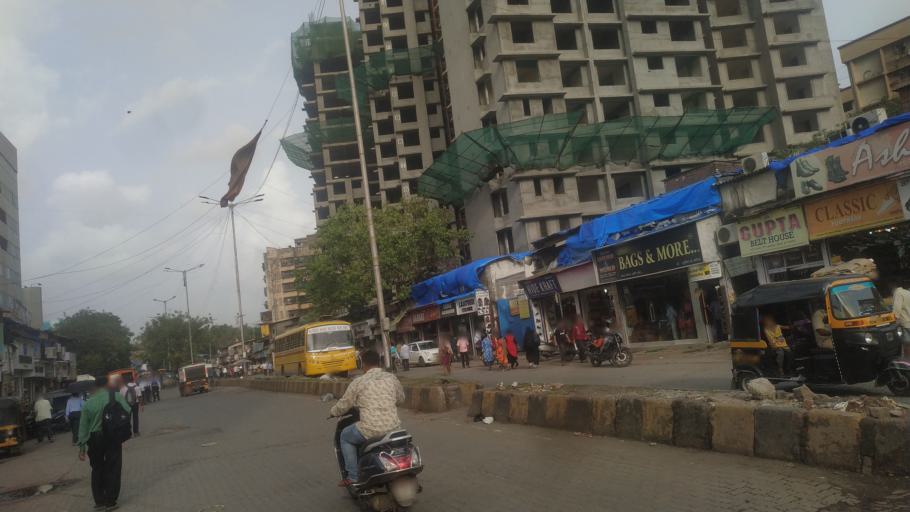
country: IN
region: Maharashtra
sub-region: Mumbai Suburban
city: Mumbai
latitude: 19.0481
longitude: 72.8583
